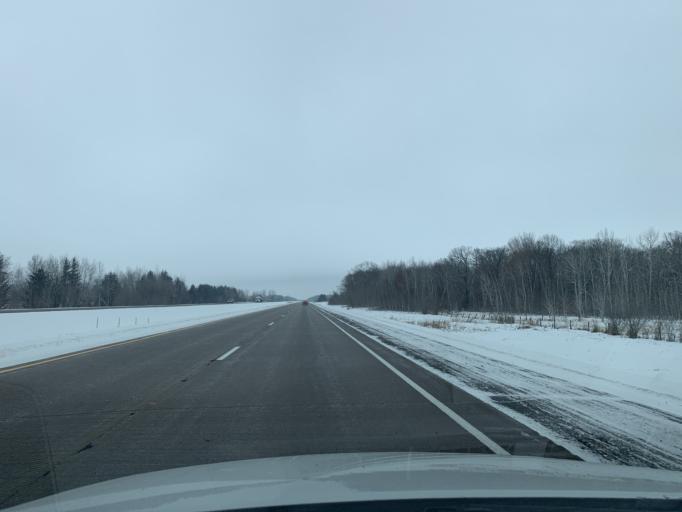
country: US
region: Minnesota
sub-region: Chisago County
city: Harris
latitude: 45.6360
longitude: -92.9921
